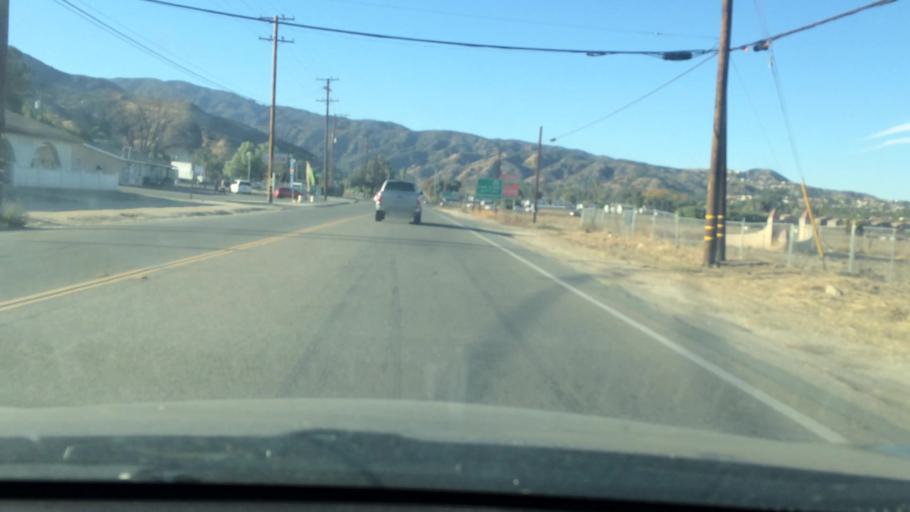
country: US
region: California
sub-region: Riverside County
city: Lakeland Village
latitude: 33.6622
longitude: -117.3820
